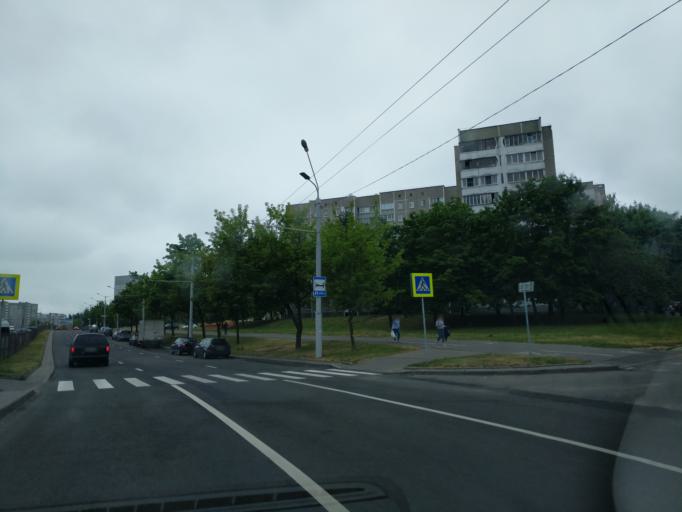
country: BY
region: Minsk
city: Novoye Medvezhino
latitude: 53.8624
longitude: 27.4656
